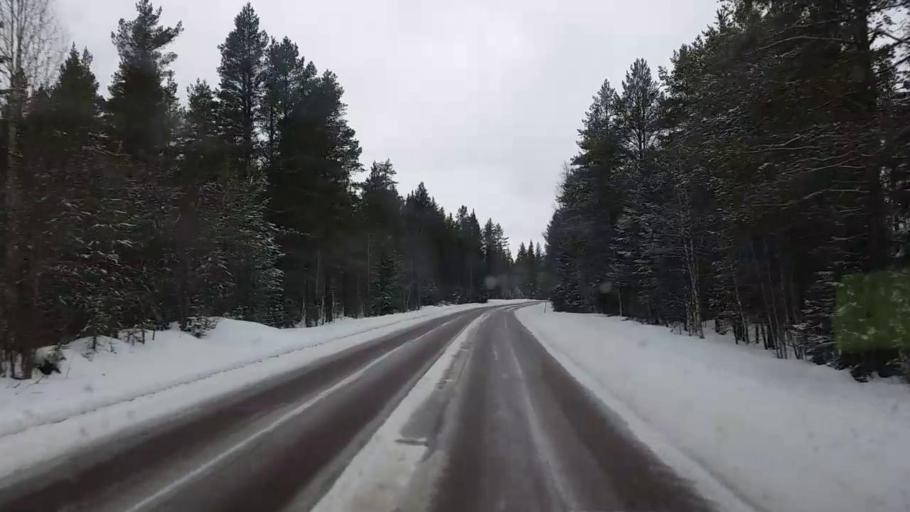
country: SE
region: Jaemtland
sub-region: Bergs Kommun
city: Hoverberg
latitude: 62.4222
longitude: 14.6050
